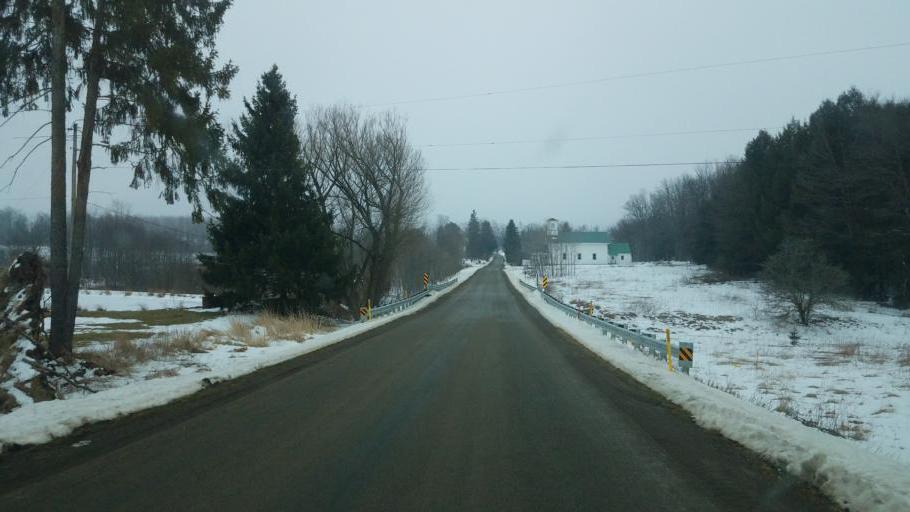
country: US
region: New York
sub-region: Allegany County
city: Andover
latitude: 41.9932
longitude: -77.7624
